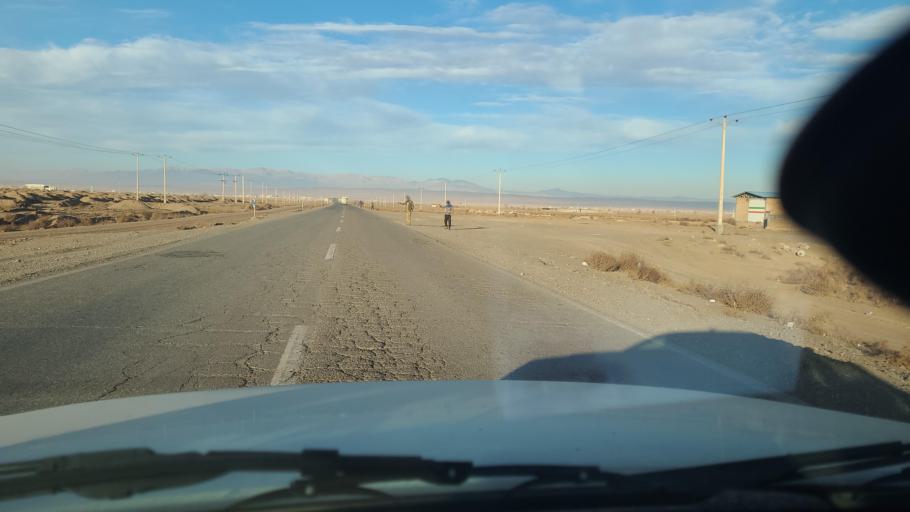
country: IR
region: Razavi Khorasan
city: Neqab
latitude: 36.5900
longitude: 57.5843
